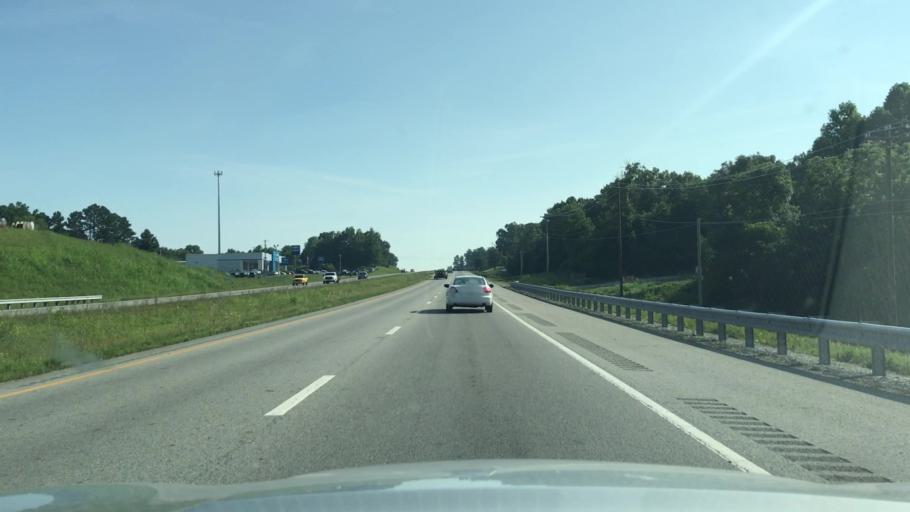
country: US
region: Tennessee
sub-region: Overton County
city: Livingston
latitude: 36.3338
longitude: -85.3533
